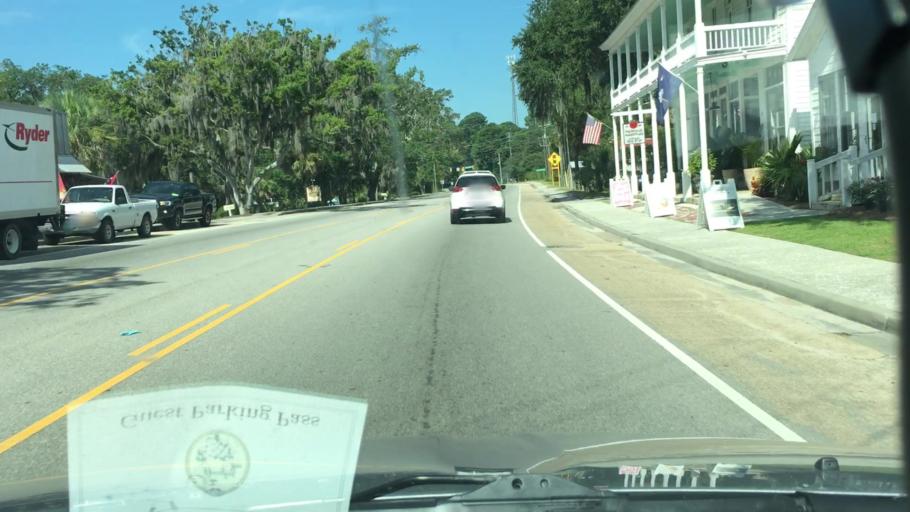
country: US
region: South Carolina
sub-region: Beaufort County
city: Beaufort
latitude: 32.3968
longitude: -80.5778
